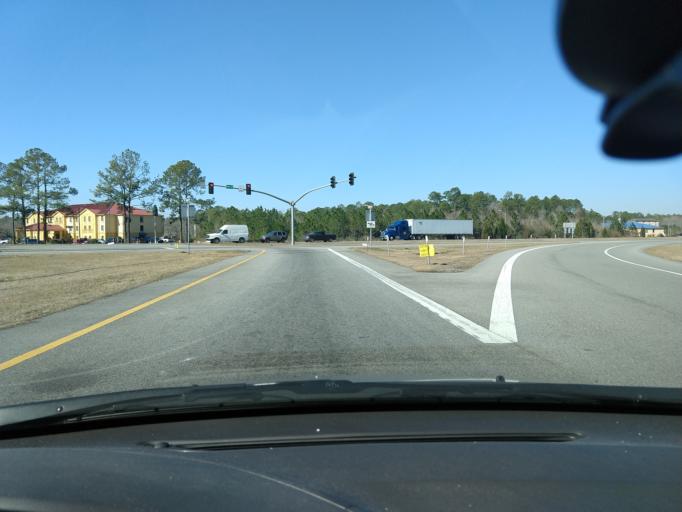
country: US
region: Mississippi
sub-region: Jackson County
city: Escatawpa
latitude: 30.4432
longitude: -88.5286
